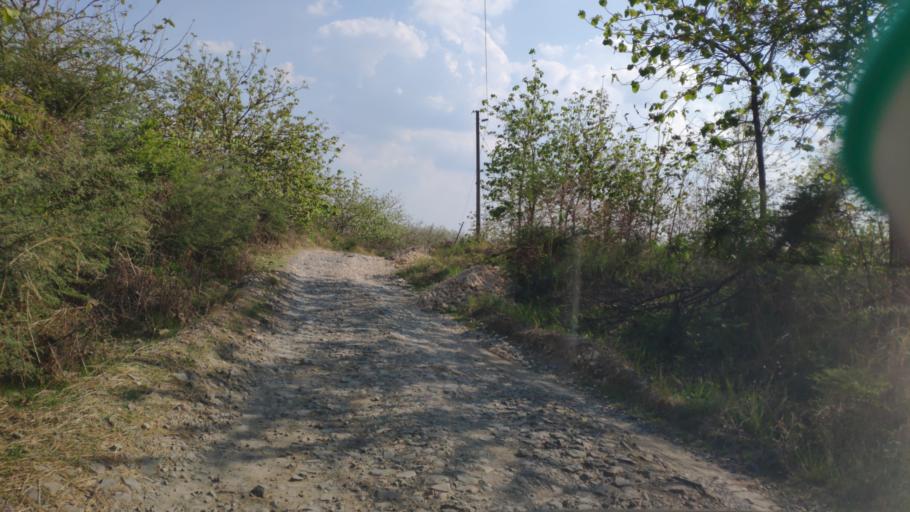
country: ID
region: Central Java
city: Randublatung
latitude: -7.2218
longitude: 111.3476
